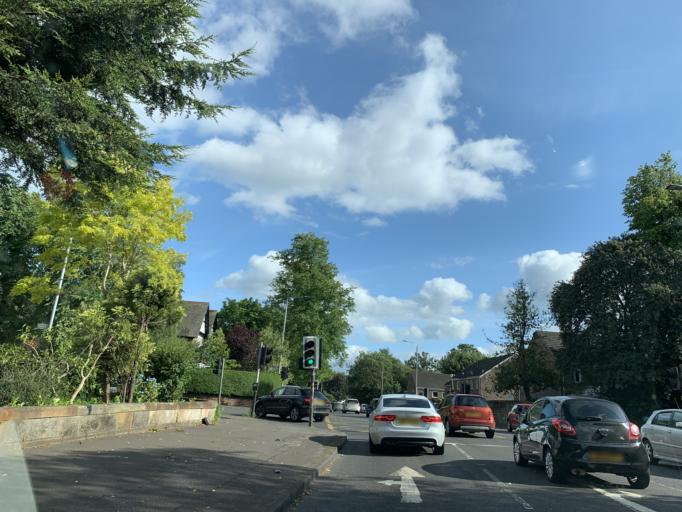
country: GB
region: Scotland
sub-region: East Renfrewshire
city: Giffnock
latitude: 55.8449
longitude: -4.3097
